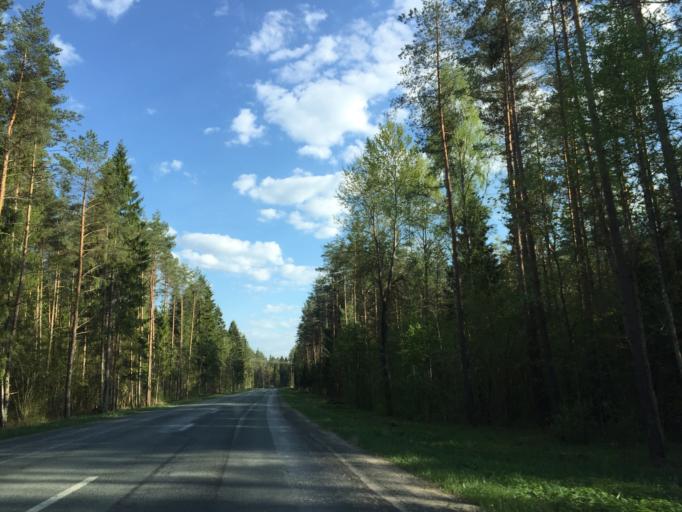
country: LV
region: Sigulda
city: Sigulda
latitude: 57.2254
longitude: 24.8530
